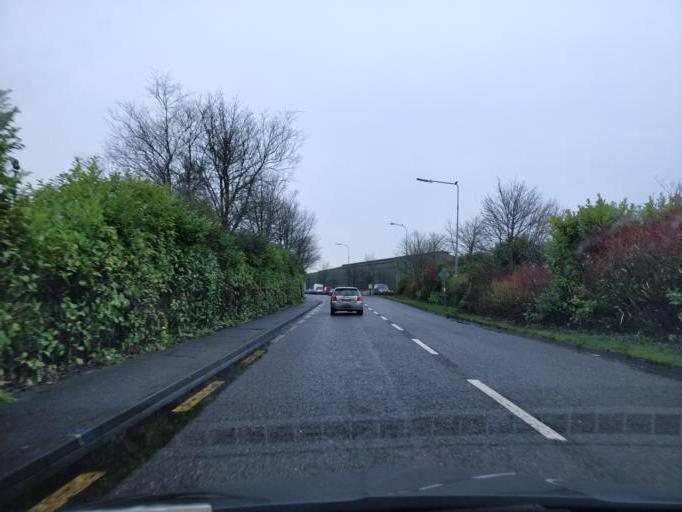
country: IE
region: Connaught
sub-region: Maigh Eo
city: Ballyhaunis
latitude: 53.7580
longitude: -8.7721
